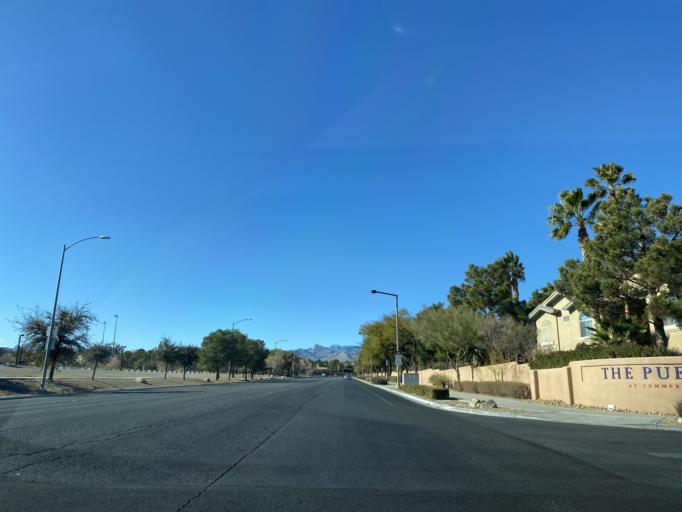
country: US
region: Nevada
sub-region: Clark County
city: Summerlin South
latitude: 36.1887
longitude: -115.2831
